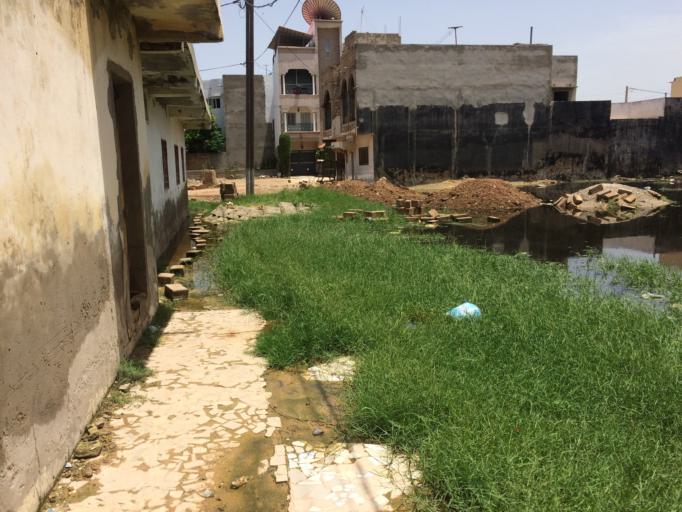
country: SN
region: Dakar
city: Pikine
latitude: 14.7371
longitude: -17.3320
